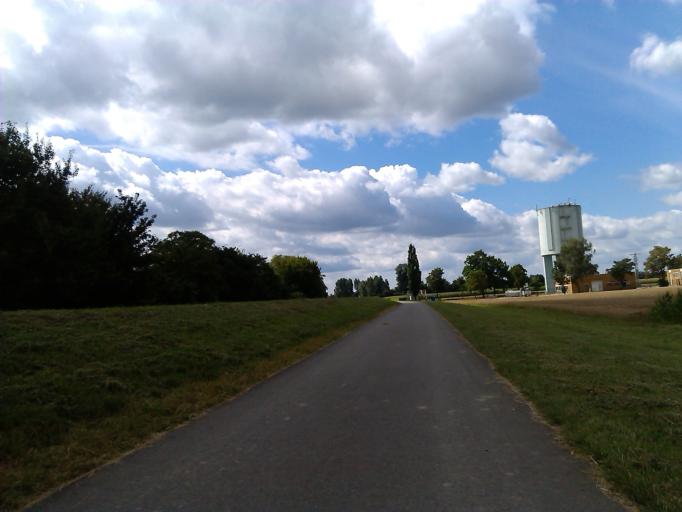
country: DE
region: Rheinland-Pfalz
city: Otterstadt
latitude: 49.3862
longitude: 8.4582
